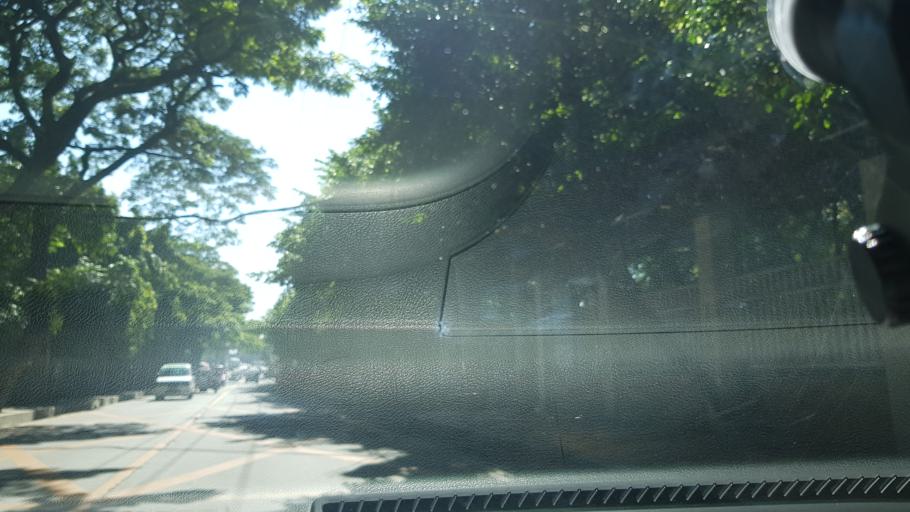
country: PH
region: Calabarzon
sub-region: Province of Rizal
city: Cainta
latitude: 14.5755
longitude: 121.0966
